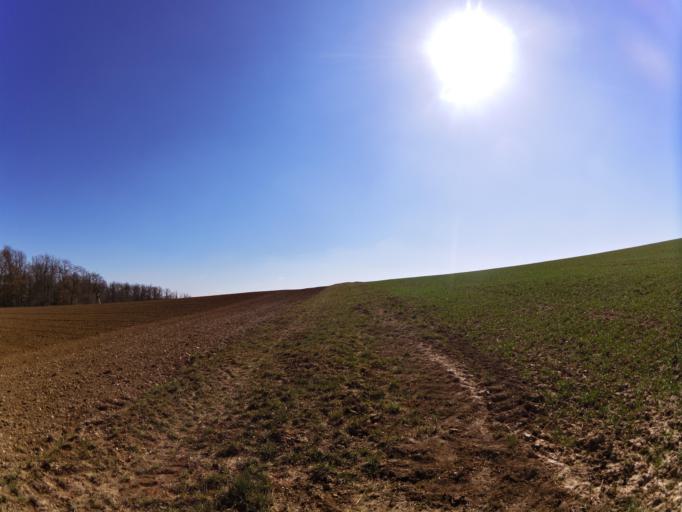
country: DE
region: Bavaria
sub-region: Regierungsbezirk Unterfranken
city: Greussenheim
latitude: 49.8058
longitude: 9.7812
